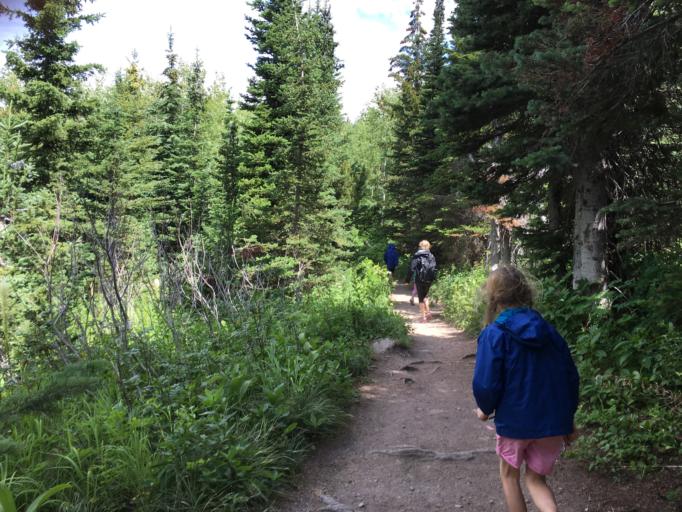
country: CA
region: Alberta
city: Cardston
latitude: 48.7945
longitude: -113.6585
